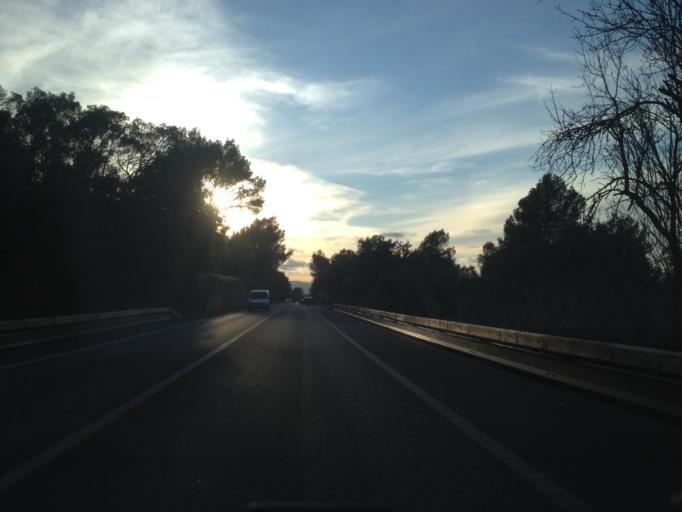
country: ES
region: Balearic Islands
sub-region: Illes Balears
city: Marratxi
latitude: 39.6475
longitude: 2.7520
